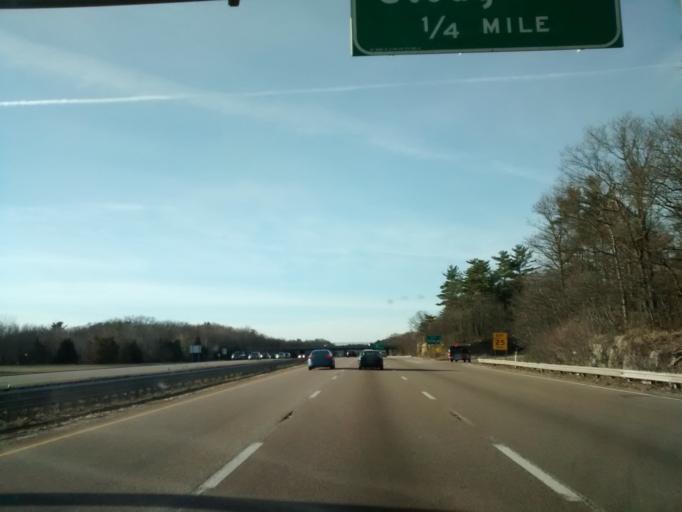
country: US
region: Massachusetts
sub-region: Norfolk County
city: Randolph
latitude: 42.1539
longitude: -71.0681
